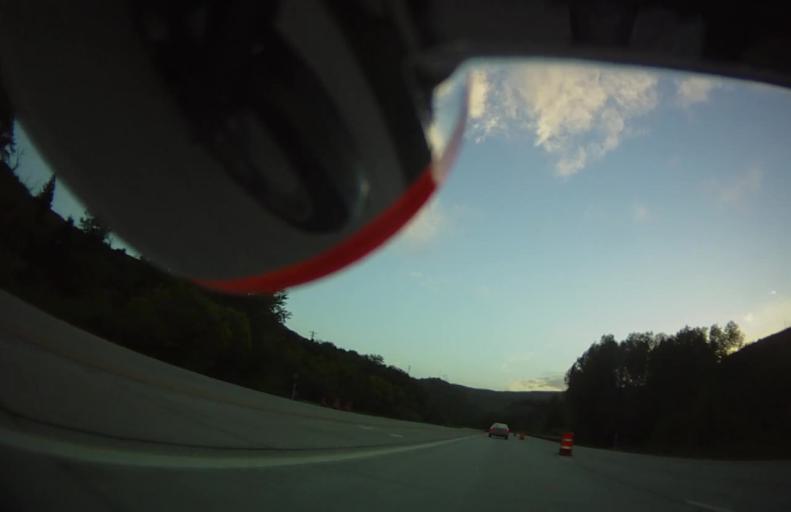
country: US
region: Utah
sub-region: Utah County
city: Orem
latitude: 40.3287
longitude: -111.6240
